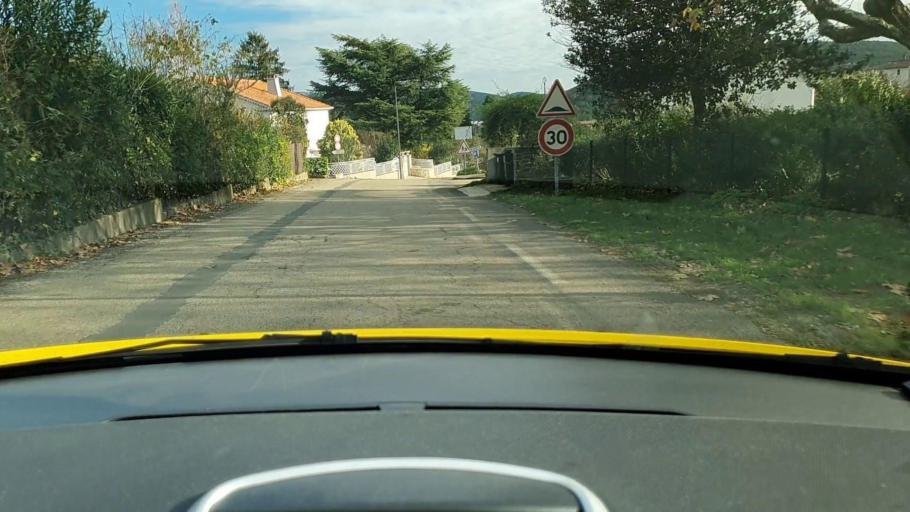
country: FR
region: Languedoc-Roussillon
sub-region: Departement du Gard
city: Branoux-les-Taillades
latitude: 44.2207
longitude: 3.9901
